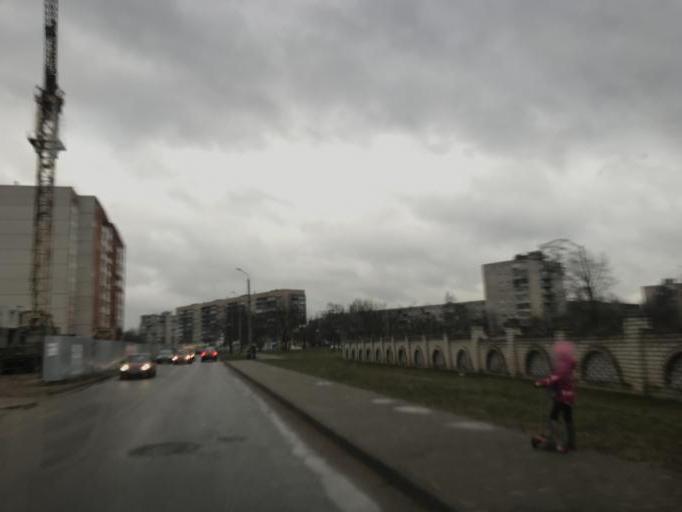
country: BY
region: Mogilev
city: Mahilyow
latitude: 53.8803
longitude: 30.3257
